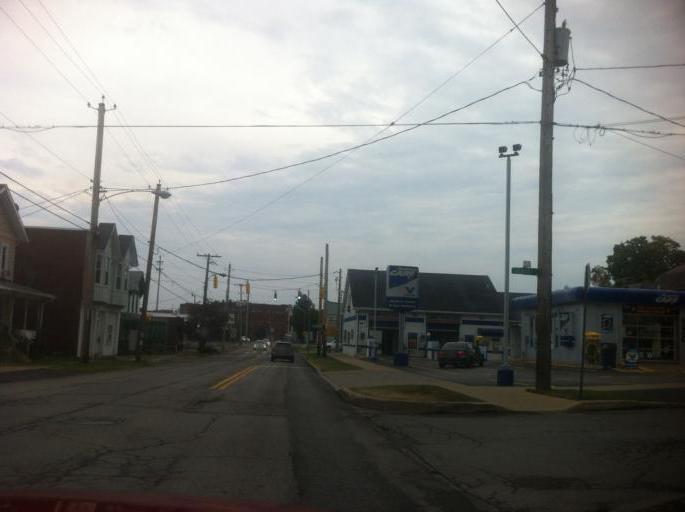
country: US
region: Pennsylvania
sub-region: Mercer County
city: Grove City
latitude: 41.1628
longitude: -80.0849
